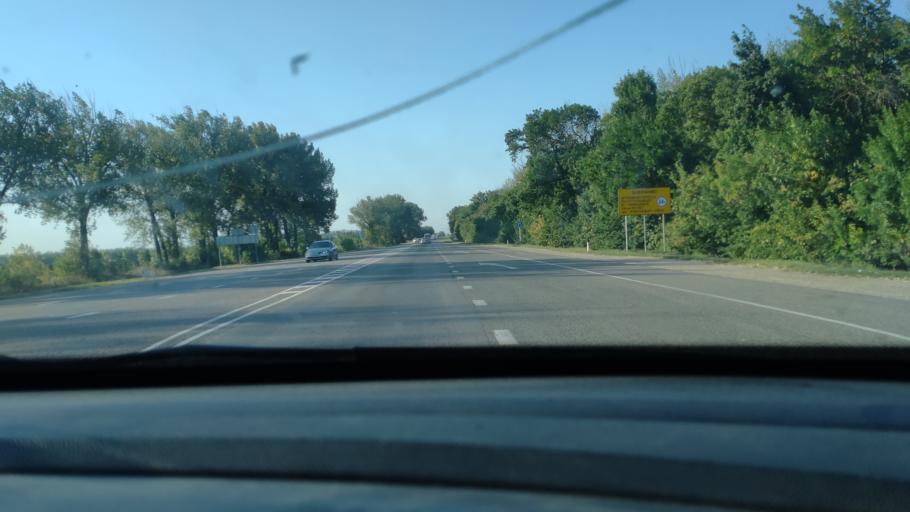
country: RU
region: Krasnodarskiy
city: Medvedovskaya
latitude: 45.4541
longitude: 38.9895
